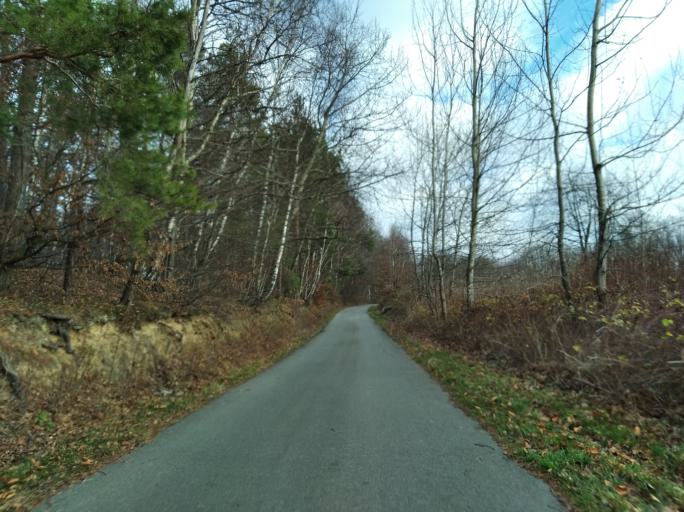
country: PL
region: Subcarpathian Voivodeship
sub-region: Powiat strzyzowski
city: Strzyzow
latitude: 49.8822
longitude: 21.8348
